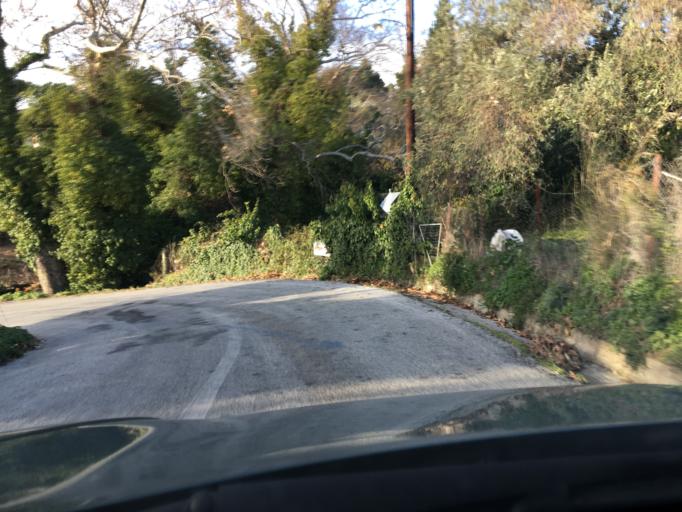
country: GR
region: Thessaly
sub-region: Nomos Magnisias
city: Skopelos
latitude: 39.1684
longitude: 23.6166
